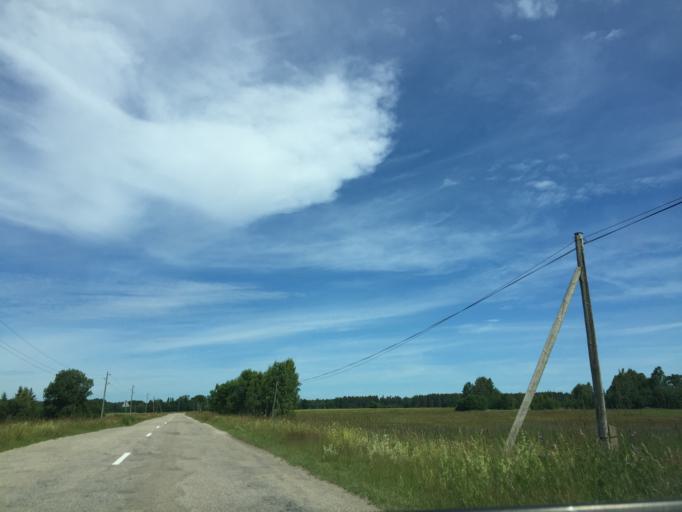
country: LV
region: Dundaga
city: Dundaga
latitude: 57.5276
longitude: 22.3303
